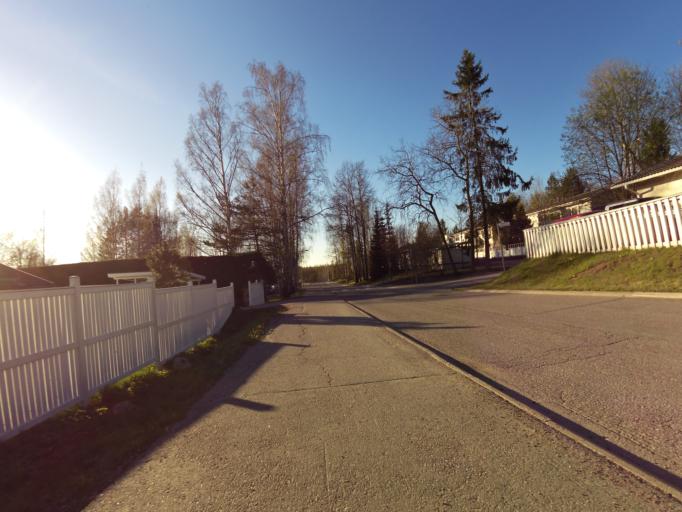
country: FI
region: Uusimaa
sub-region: Helsinki
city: Espoo
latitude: 60.1675
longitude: 24.6686
